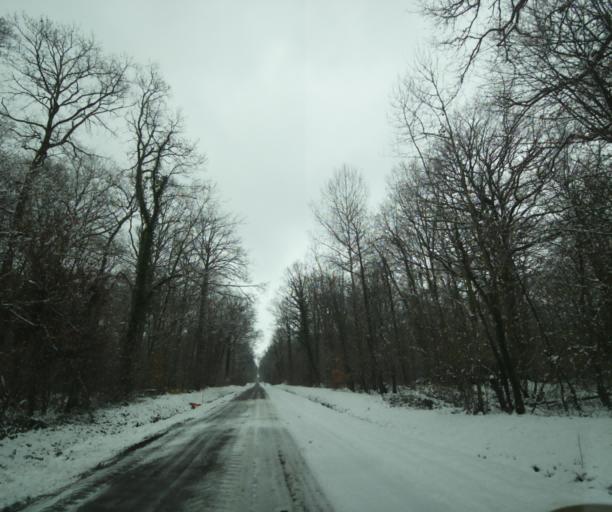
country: FR
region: Champagne-Ardenne
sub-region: Departement de la Haute-Marne
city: Laneuville-a-Remy
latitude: 48.3949
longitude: 4.8669
